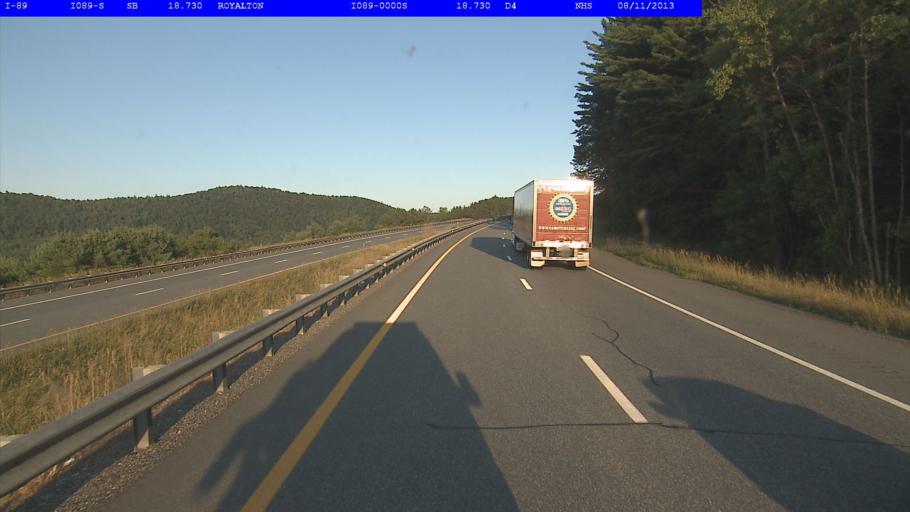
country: US
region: Vermont
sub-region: Orange County
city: Randolph
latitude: 43.8225
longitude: -72.5306
